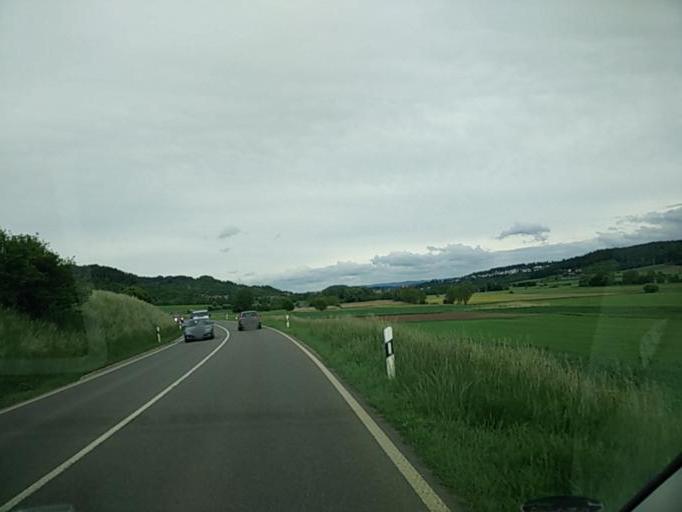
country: DE
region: Baden-Wuerttemberg
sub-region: Tuebingen Region
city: Tuebingen
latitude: 48.5234
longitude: 9.0006
